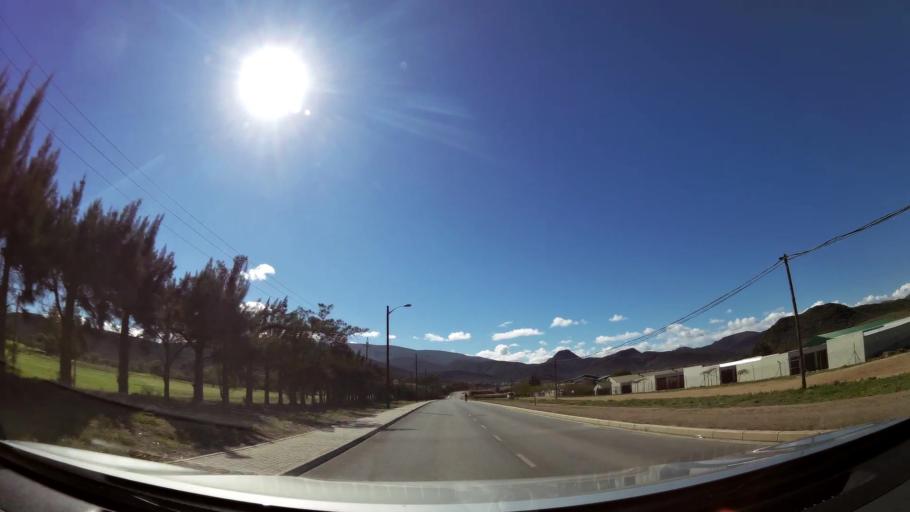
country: ZA
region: Western Cape
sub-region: Cape Winelands District Municipality
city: Ashton
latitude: -33.7753
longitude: 20.1332
